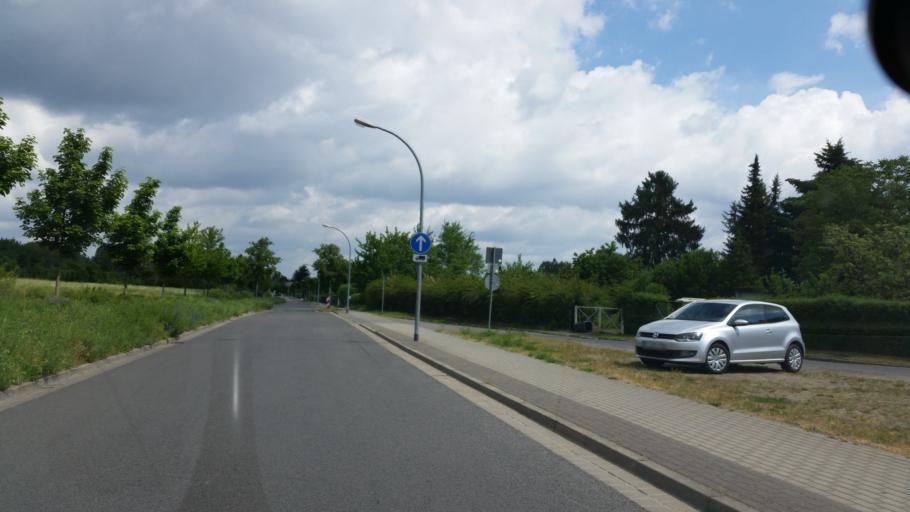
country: DE
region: Brandenburg
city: Grossbeeren
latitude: 52.3910
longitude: 13.3024
